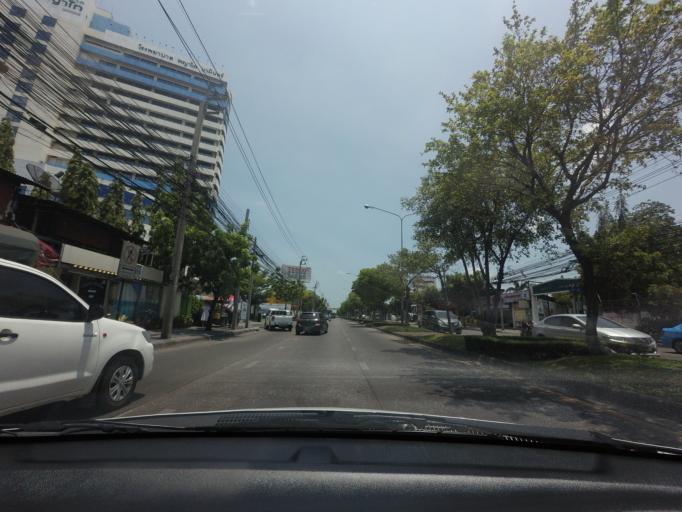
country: TH
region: Bangkok
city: Khan Na Yao
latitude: 13.8258
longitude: 100.6570
